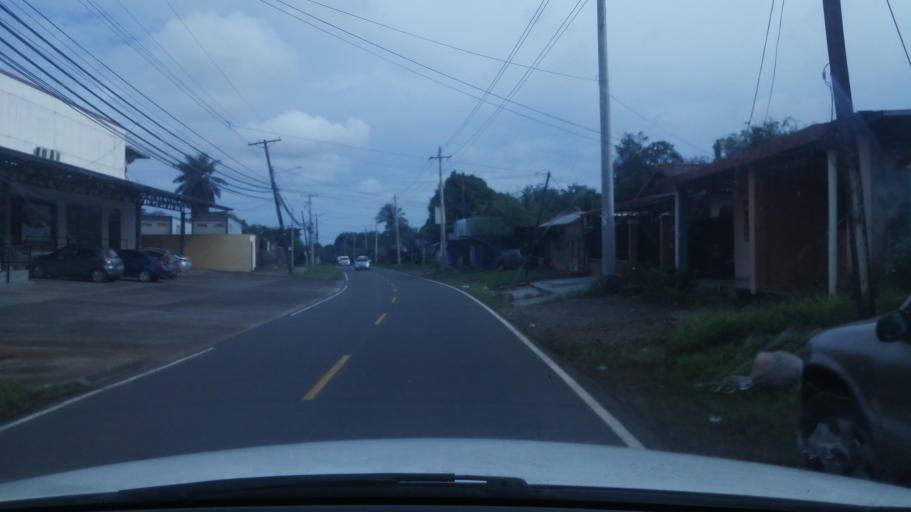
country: PA
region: Chiriqui
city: David
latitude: 8.4184
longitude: -82.4260
